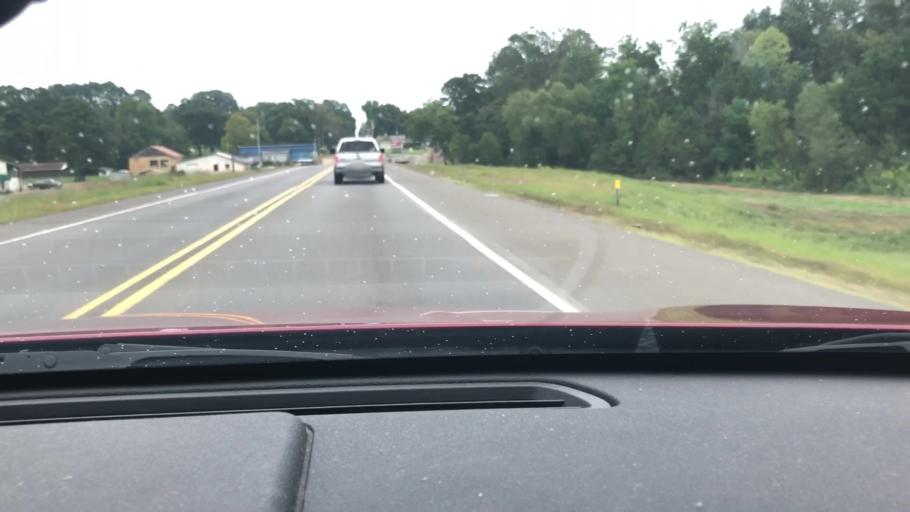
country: US
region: Arkansas
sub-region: Lafayette County
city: Stamps
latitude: 33.3657
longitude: -93.5015
